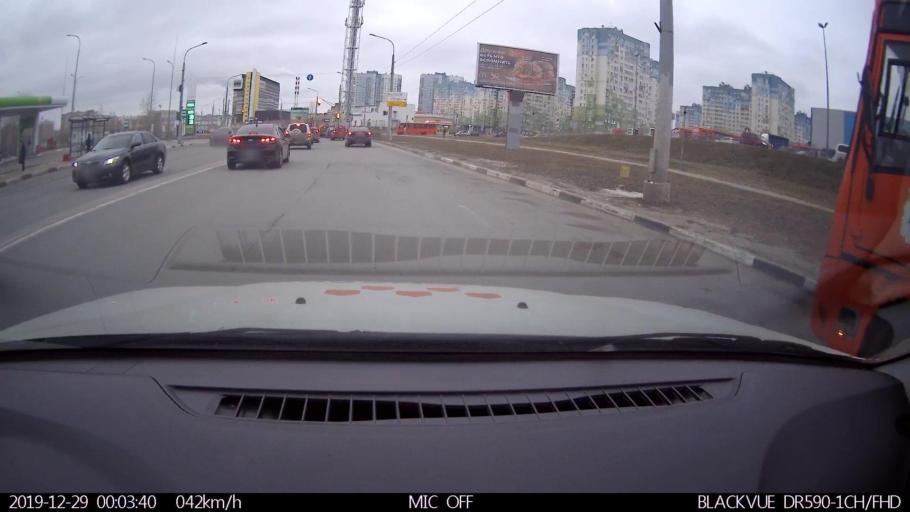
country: RU
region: Nizjnij Novgorod
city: Nizhniy Novgorod
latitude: 56.3377
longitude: 43.9535
